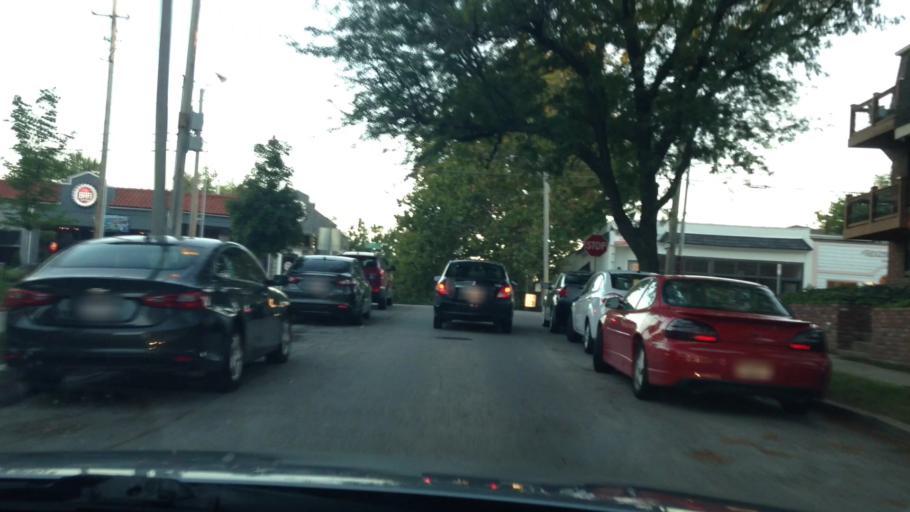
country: US
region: Kansas
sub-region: Johnson County
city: Westwood
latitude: 39.0430
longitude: -94.6008
